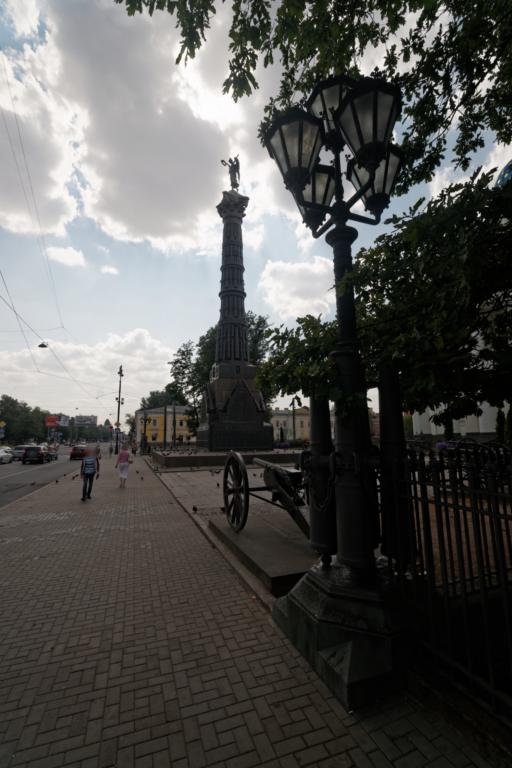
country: RU
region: St.-Petersburg
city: Saint Petersburg
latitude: 59.9168
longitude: 30.3073
